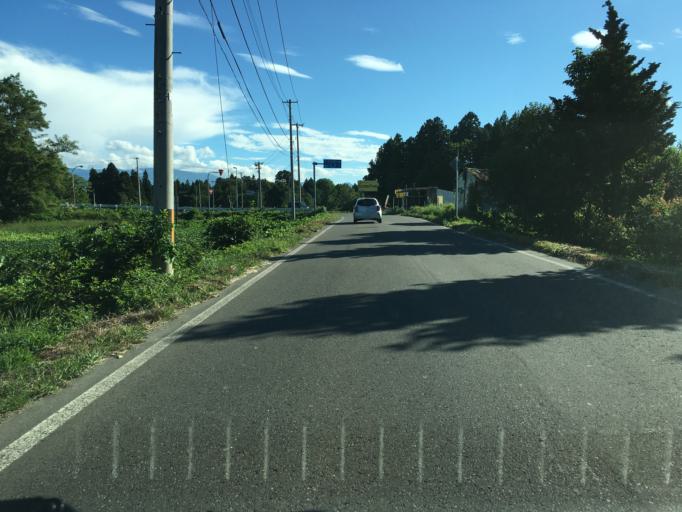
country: JP
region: Yamagata
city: Yonezawa
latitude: 37.9519
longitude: 140.1387
